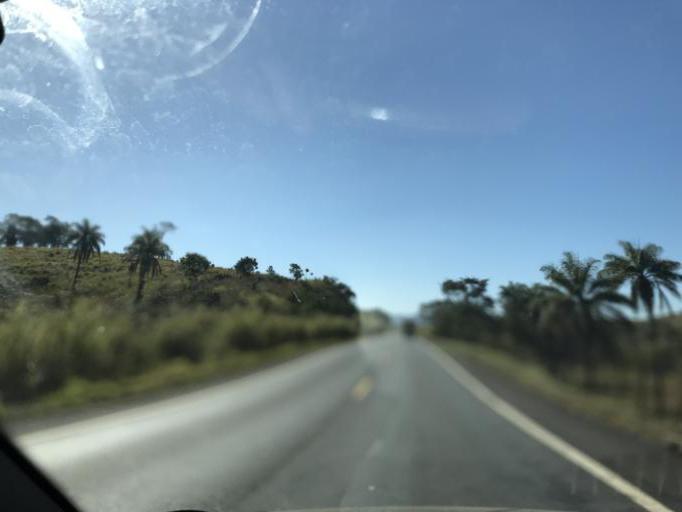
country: BR
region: Minas Gerais
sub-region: Bambui
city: Bambui
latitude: -19.8625
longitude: -45.9859
